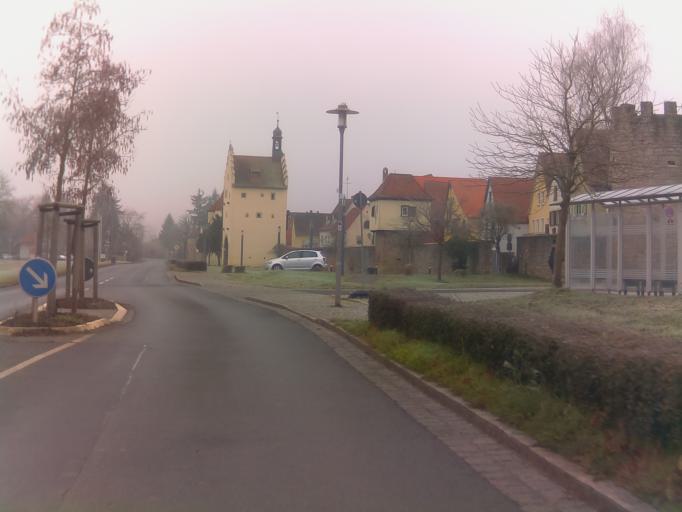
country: DE
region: Bavaria
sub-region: Regierungsbezirk Unterfranken
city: Sulzfeld am Main
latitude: 49.7092
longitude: 10.1351
